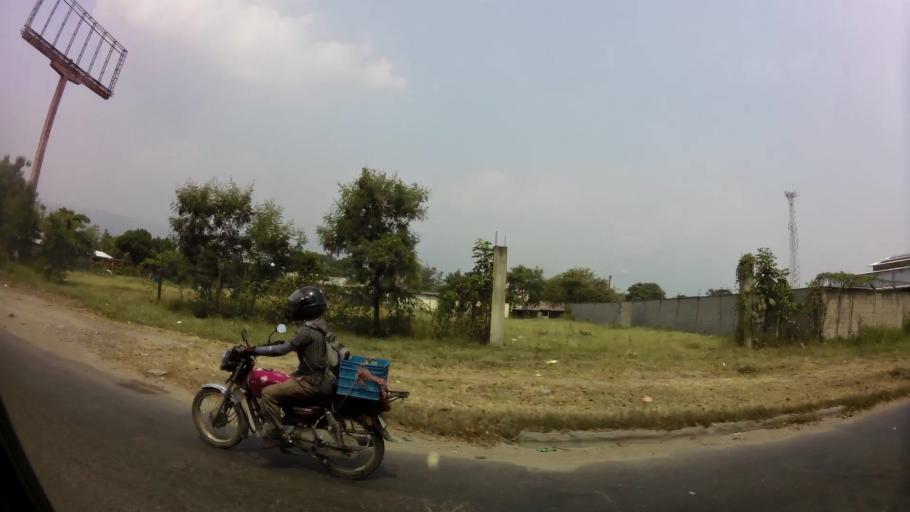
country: HN
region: Cortes
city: San Pedro Sula
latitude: 15.4777
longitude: -88.0079
